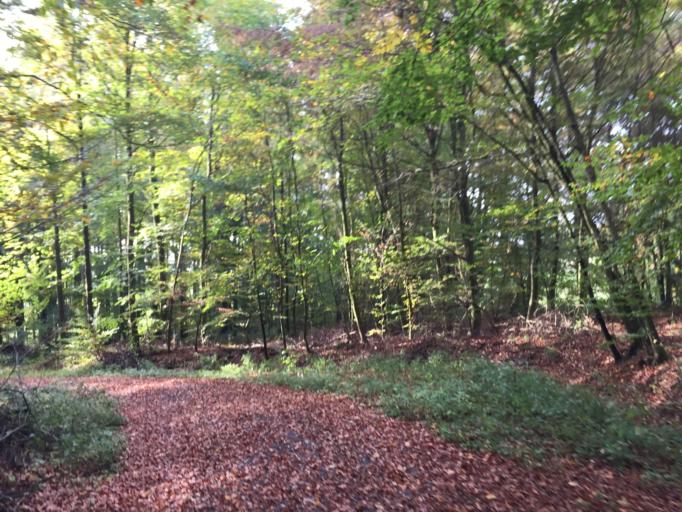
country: DE
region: Hesse
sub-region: Regierungsbezirk Giessen
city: Laubach
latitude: 50.5608
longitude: 8.9893
